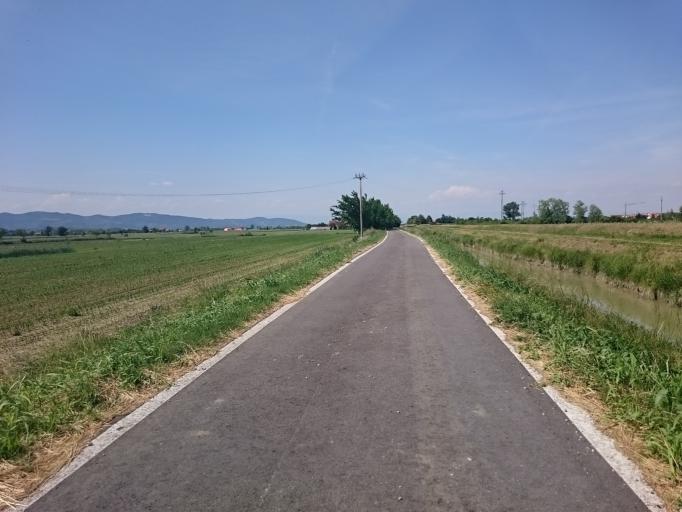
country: IT
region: Veneto
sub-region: Provincia di Padova
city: Vo
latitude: 45.3556
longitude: 11.6302
